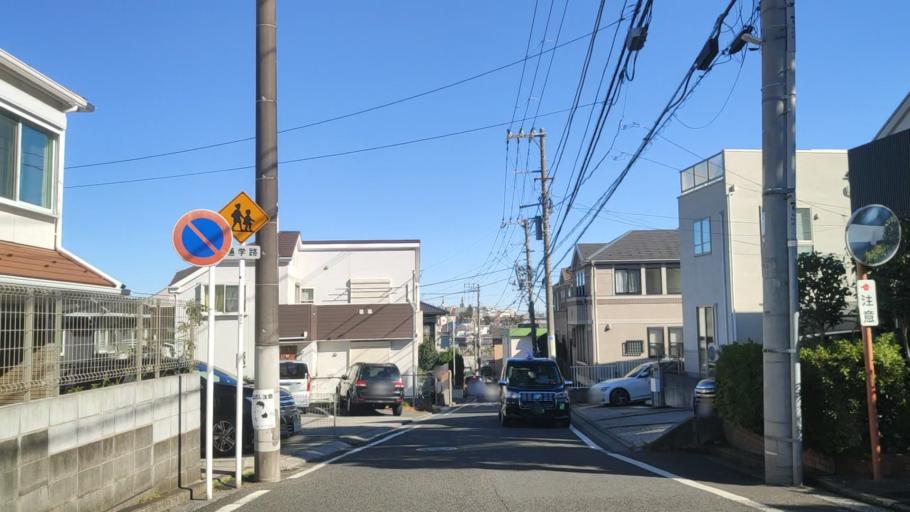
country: JP
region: Kanagawa
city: Yokohama
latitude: 35.4315
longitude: 139.6453
